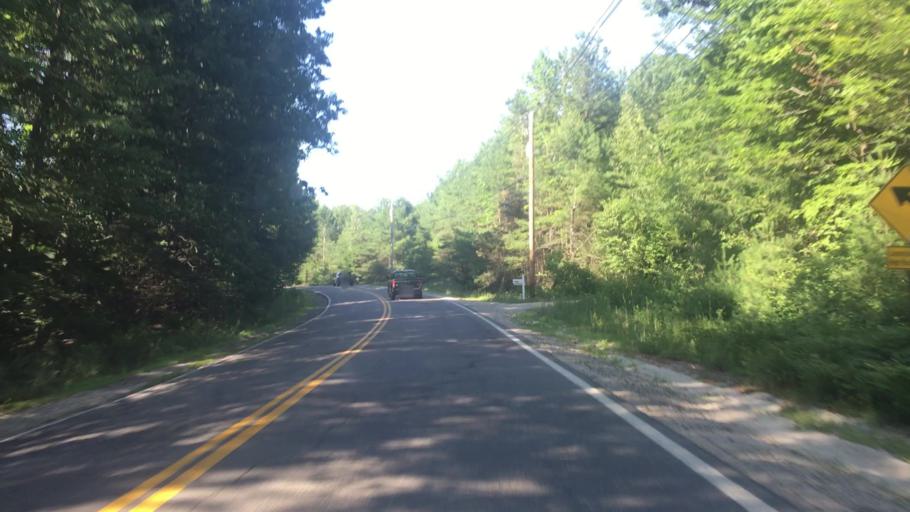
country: US
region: Maine
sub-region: York County
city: Hollis Center
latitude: 43.6808
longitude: -70.5872
